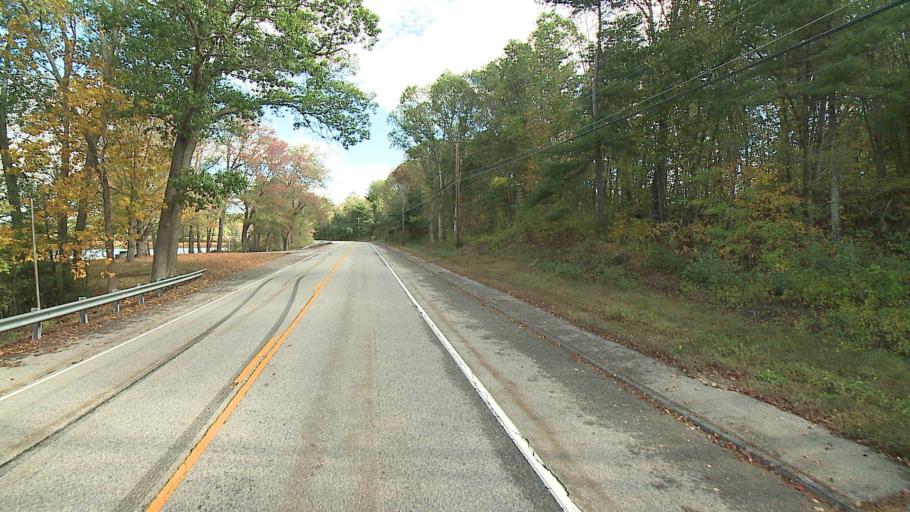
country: US
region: Connecticut
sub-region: Windham County
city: Thompson
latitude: 41.9431
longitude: -71.8906
